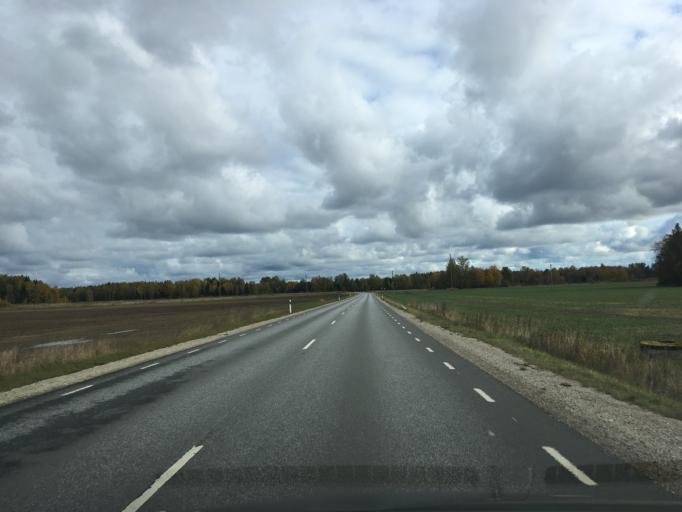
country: EE
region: Harju
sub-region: Anija vald
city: Kehra
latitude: 59.2597
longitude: 25.3424
